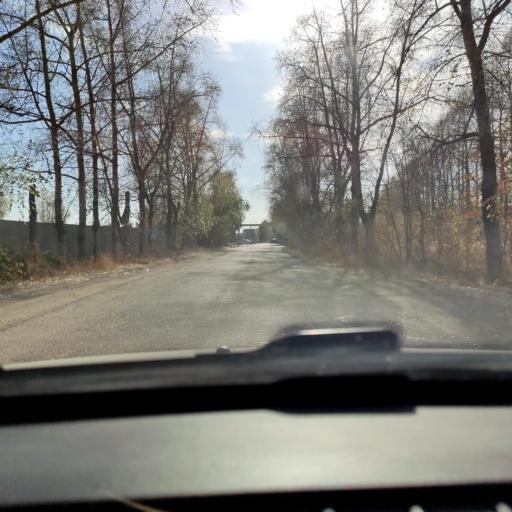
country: RU
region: Voronezj
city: Podgornoye
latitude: 51.8026
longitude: 39.1984
